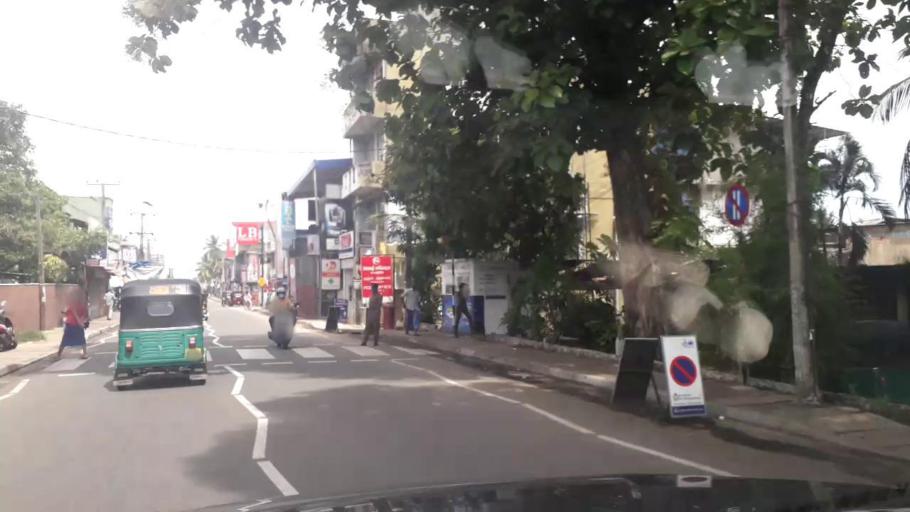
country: LK
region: Western
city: Moratuwa
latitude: 6.7499
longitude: 79.9004
